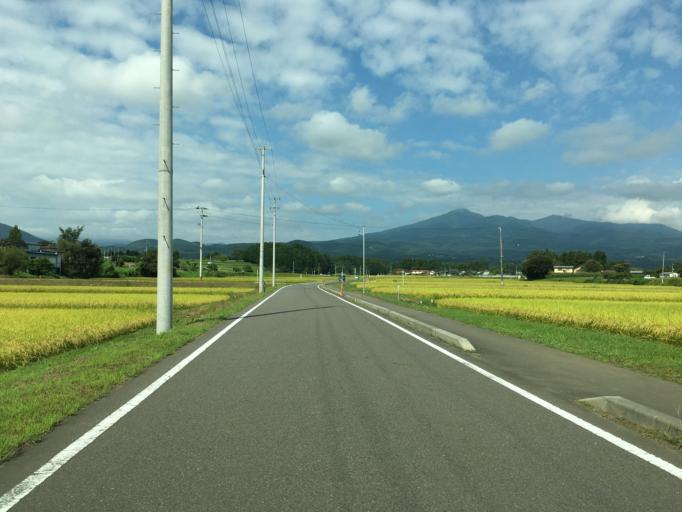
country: JP
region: Fukushima
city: Motomiya
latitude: 37.5372
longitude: 140.3673
